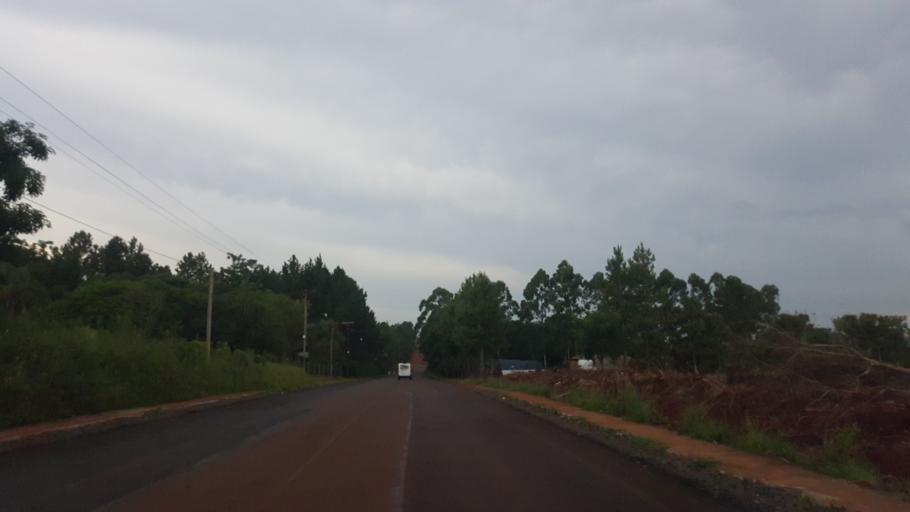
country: AR
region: Misiones
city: Puerto Leoni
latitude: -27.0036
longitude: -55.1641
